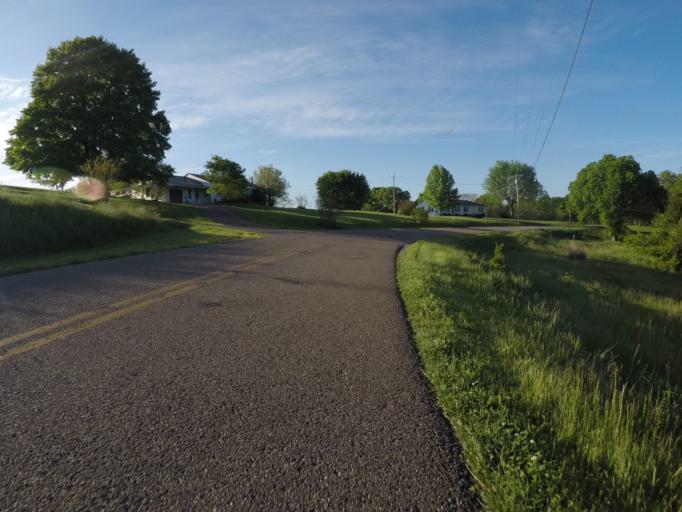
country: US
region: West Virginia
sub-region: Cabell County
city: Huntington
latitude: 38.5270
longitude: -82.4262
